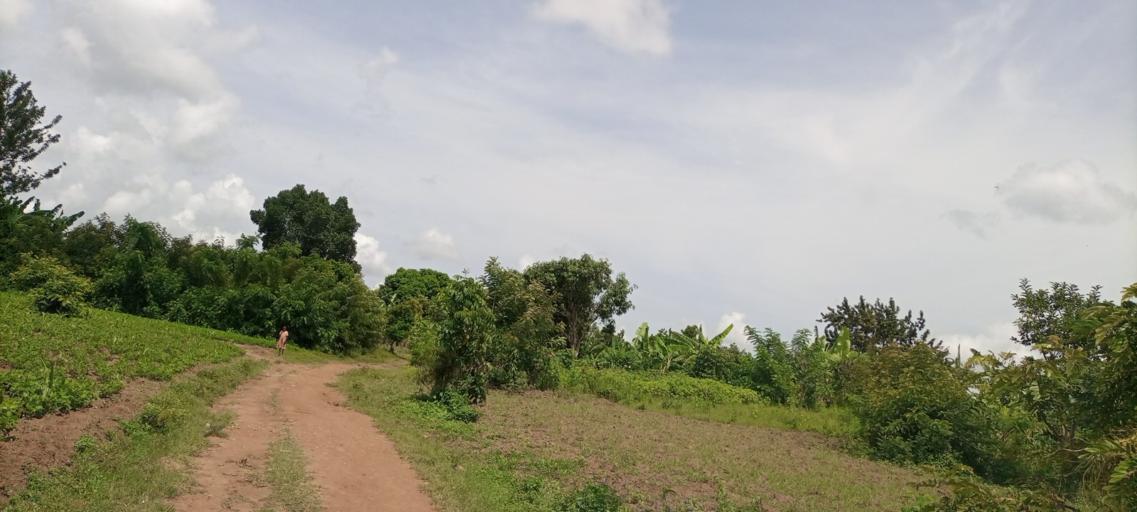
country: UG
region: Eastern Region
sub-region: Budaka District
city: Budaka
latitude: 1.1720
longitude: 33.9491
